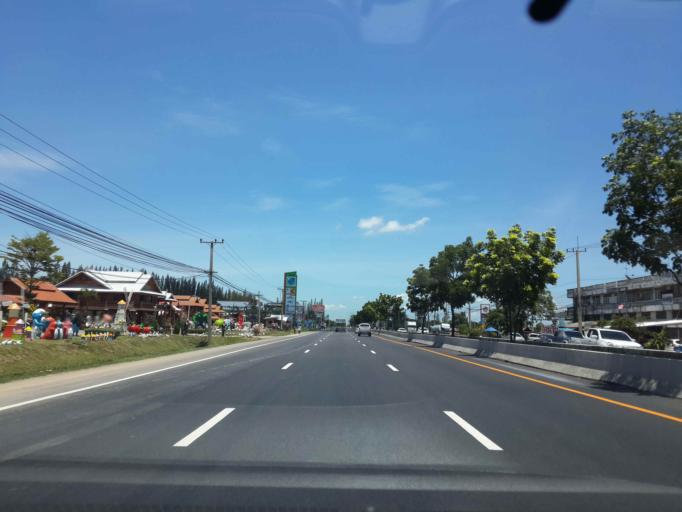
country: TH
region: Phetchaburi
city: Tha Yang
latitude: 12.8826
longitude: 99.9124
